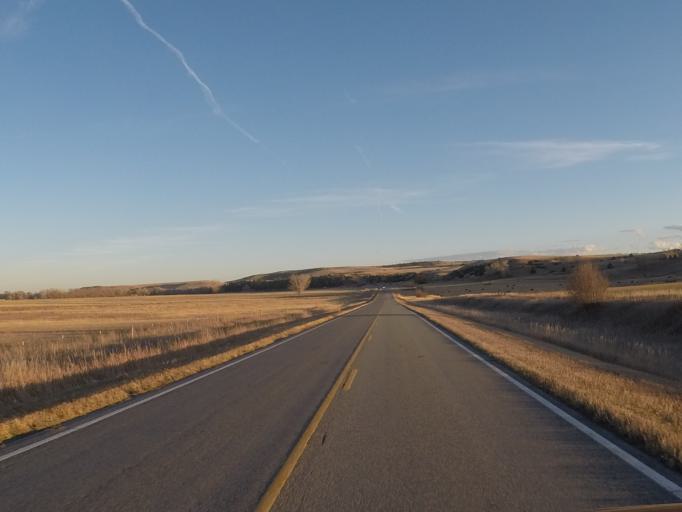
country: US
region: Montana
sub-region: Sweet Grass County
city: Big Timber
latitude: 45.7927
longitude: -109.8554
